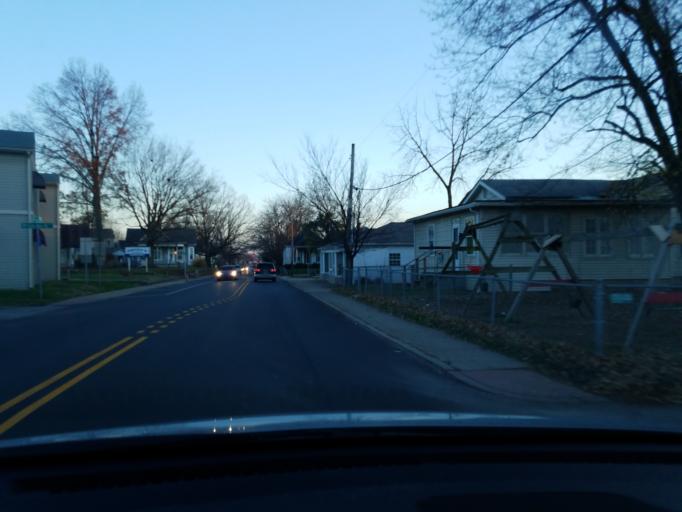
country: US
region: Indiana
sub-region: Floyd County
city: New Albany
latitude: 38.2989
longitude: -85.8022
